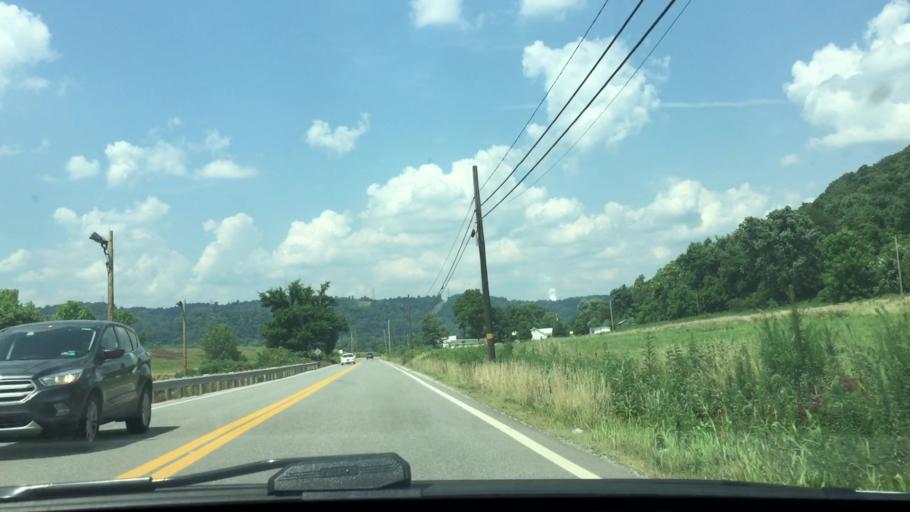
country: US
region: Ohio
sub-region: Belmont County
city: Powhatan Point
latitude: 39.7682
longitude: -80.8614
